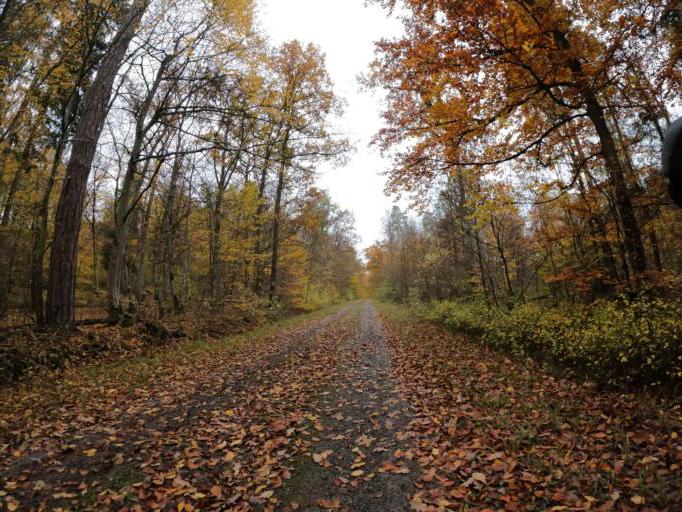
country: DE
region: Baden-Wuerttemberg
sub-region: Regierungsbezirk Stuttgart
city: Ehningen
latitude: 48.6457
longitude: 8.9471
